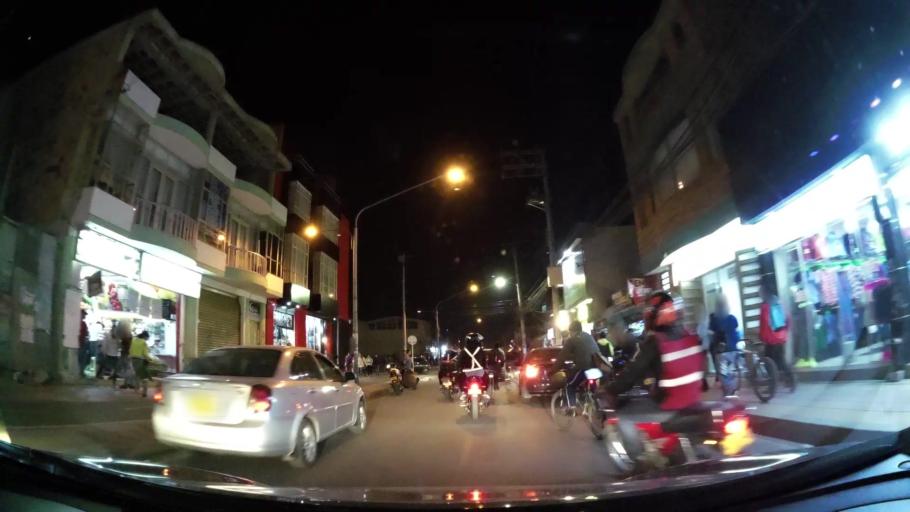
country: CO
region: Cundinamarca
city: Funza
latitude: 4.7149
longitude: -74.2150
